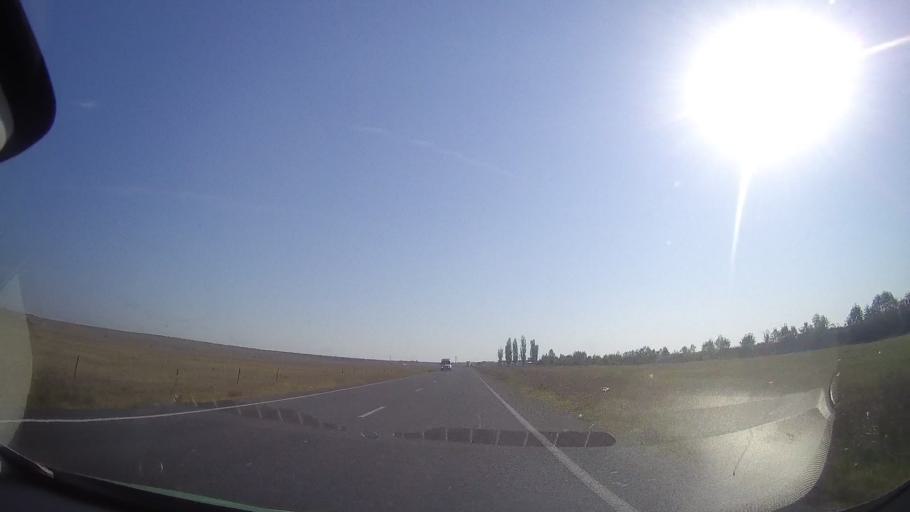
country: RO
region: Timis
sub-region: Comuna Topolovatu Mare
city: Topolovatu Mare
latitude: 45.7841
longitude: 21.5941
